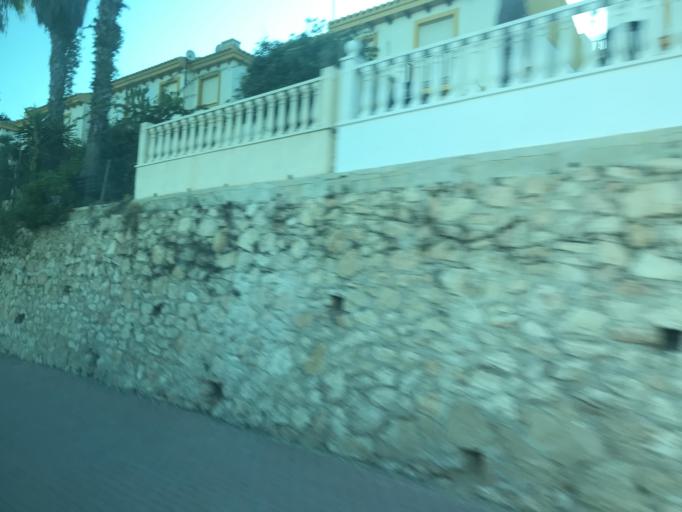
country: ES
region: Valencia
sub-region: Provincia de Alicante
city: Torrevieja
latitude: 38.0024
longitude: -0.6505
